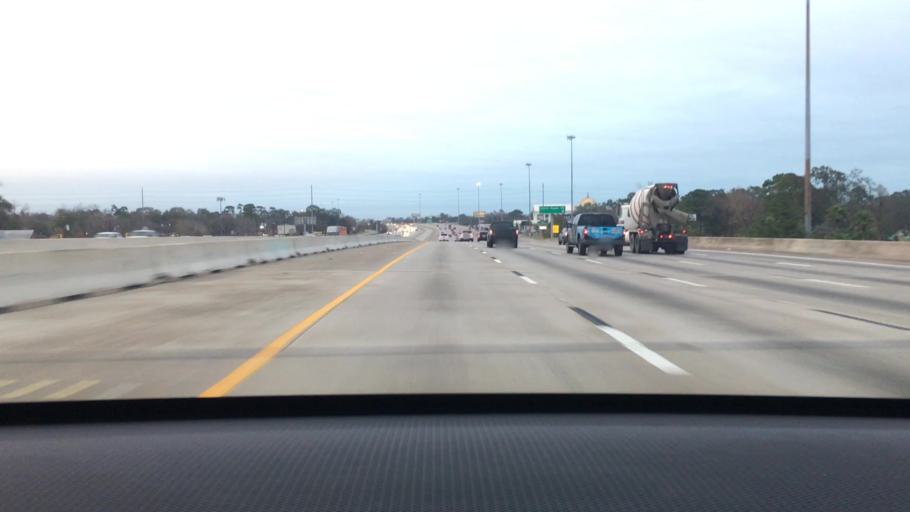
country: US
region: Texas
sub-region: Harris County
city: Houston
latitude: 29.8298
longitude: -95.3350
